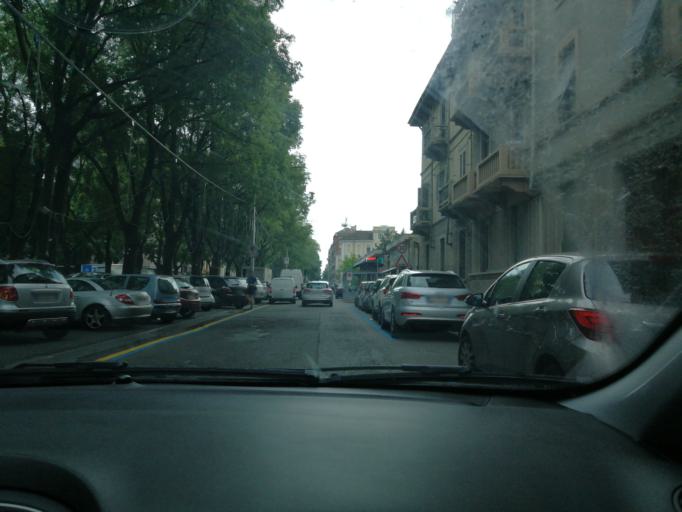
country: IT
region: Piedmont
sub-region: Provincia di Torino
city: Turin
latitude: 45.0829
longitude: 7.6512
